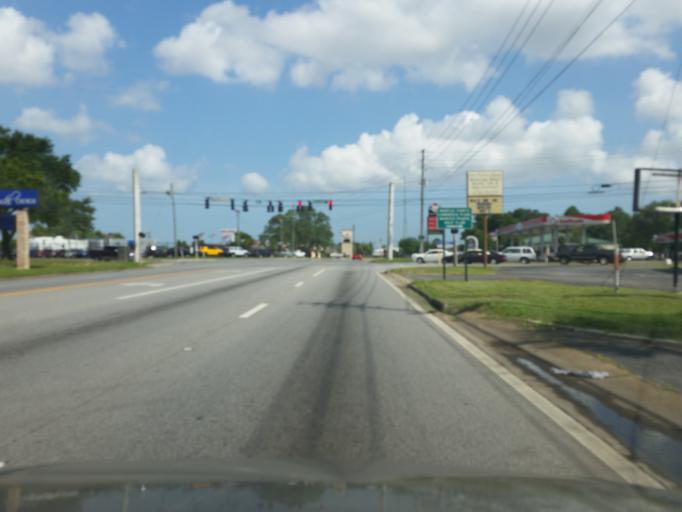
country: US
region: Florida
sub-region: Escambia County
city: Brent
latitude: 30.4819
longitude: -87.2593
